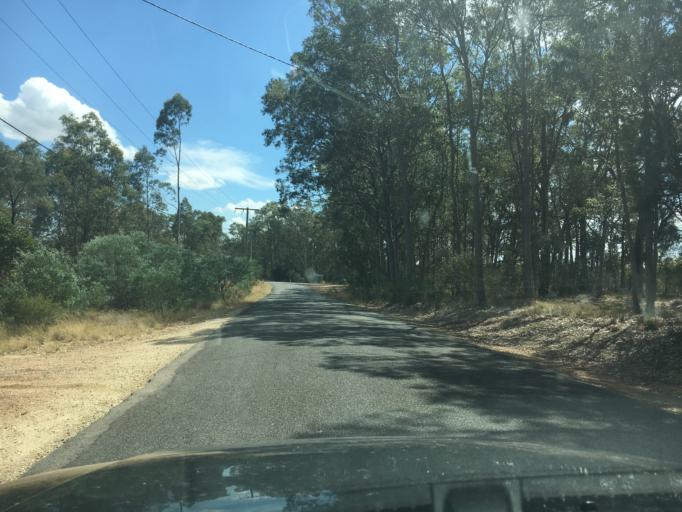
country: AU
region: New South Wales
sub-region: Singleton
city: Singleton
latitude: -32.5219
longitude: 151.1930
